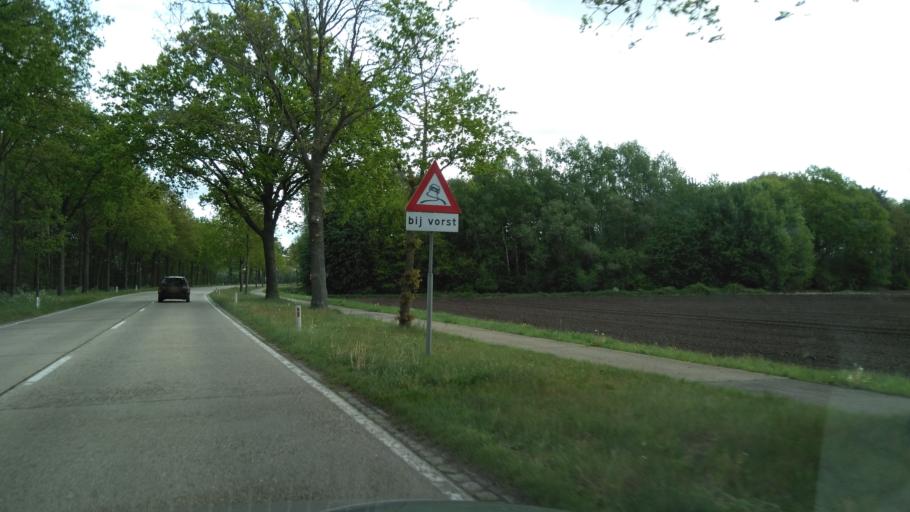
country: NL
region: North Brabant
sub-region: Gemeente Goirle
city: Goirle
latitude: 51.5089
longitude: 4.9848
